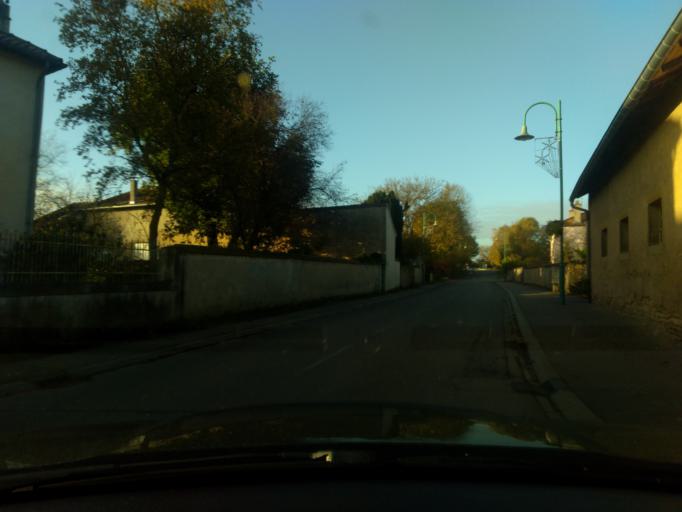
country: FR
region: Lorraine
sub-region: Departement de la Moselle
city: Marly
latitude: 49.0426
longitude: 6.1581
